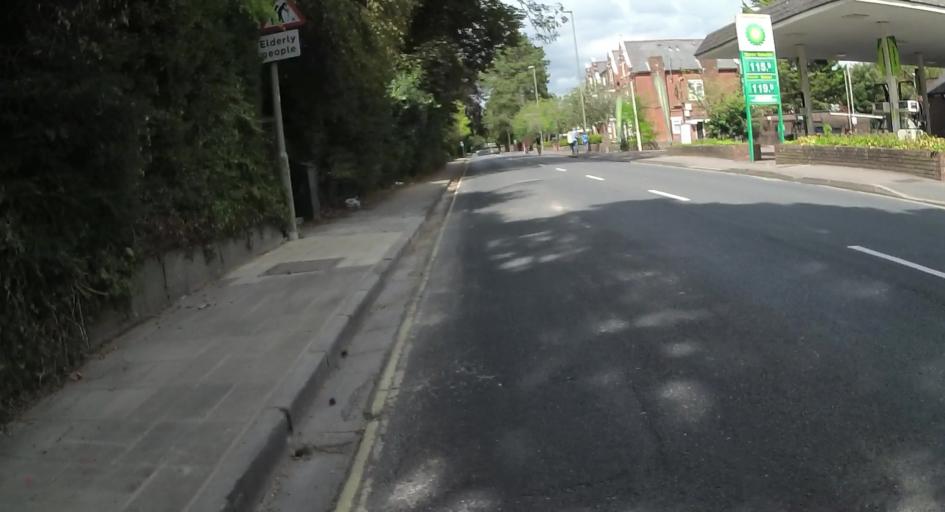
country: GB
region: England
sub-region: Hampshire
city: Winchester
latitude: 51.0537
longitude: -1.3211
